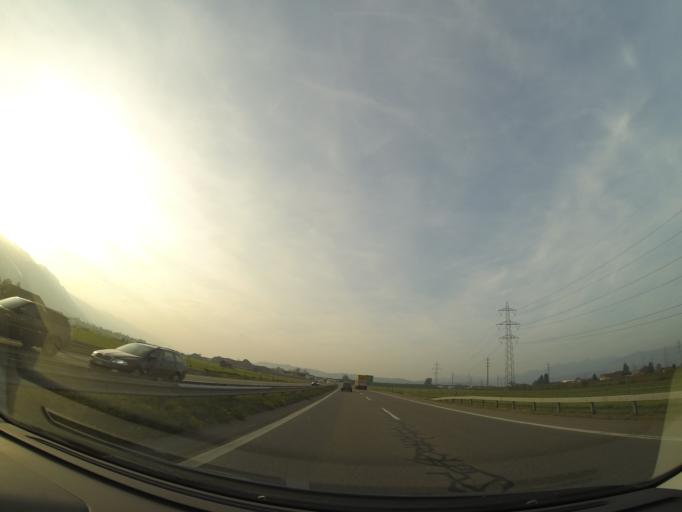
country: CH
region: Schwyz
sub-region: Bezirk March
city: Reichenburg
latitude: 47.1780
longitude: 8.9988
